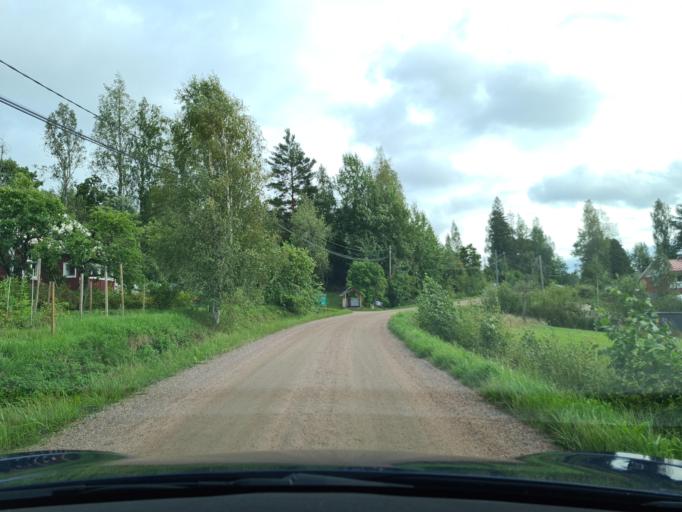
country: FI
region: Uusimaa
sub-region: Helsinki
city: Vihti
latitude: 60.4254
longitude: 24.4746
